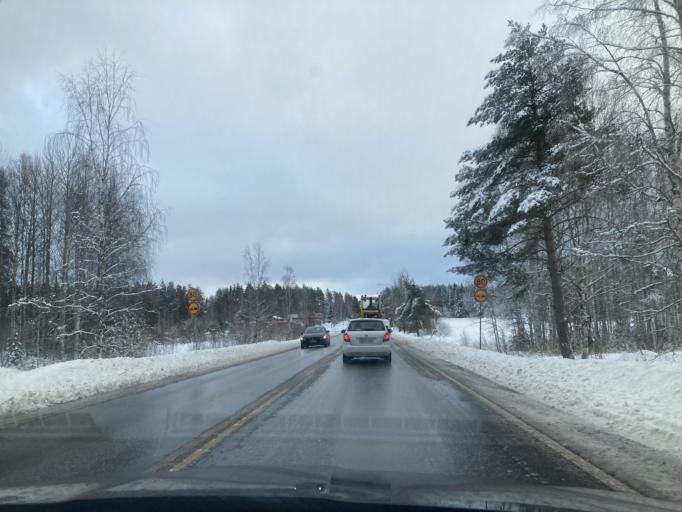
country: FI
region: Paijanne Tavastia
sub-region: Lahti
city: Padasjoki
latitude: 61.3549
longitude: 25.2278
